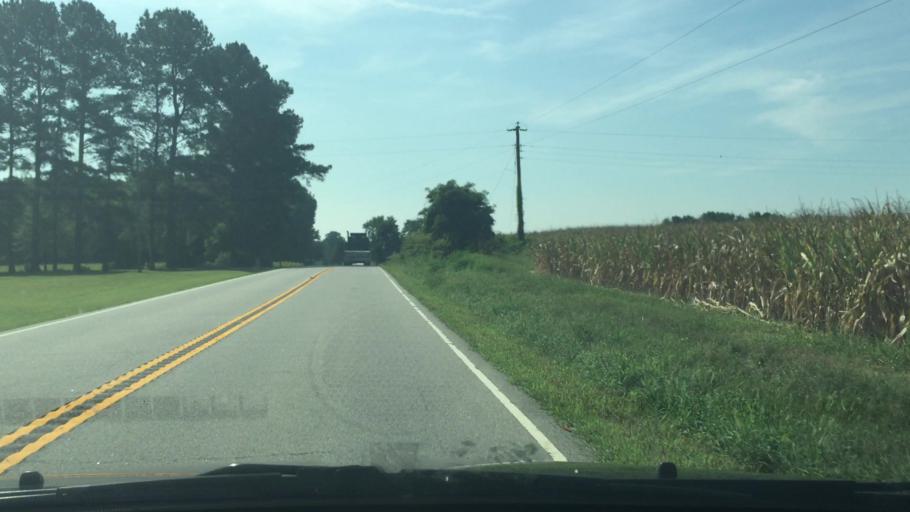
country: US
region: Virginia
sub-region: Sussex County
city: Sussex
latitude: 36.8823
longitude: -77.1529
